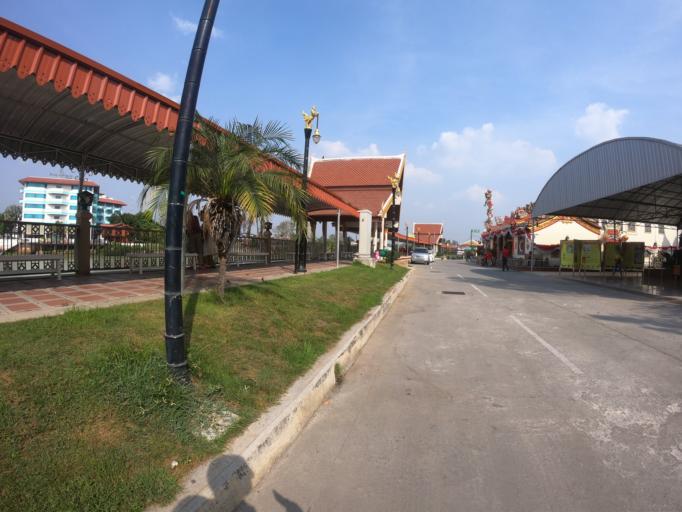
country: TH
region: Phra Nakhon Si Ayutthaya
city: Phra Nakhon Si Ayutthaya
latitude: 14.3446
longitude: 100.5788
